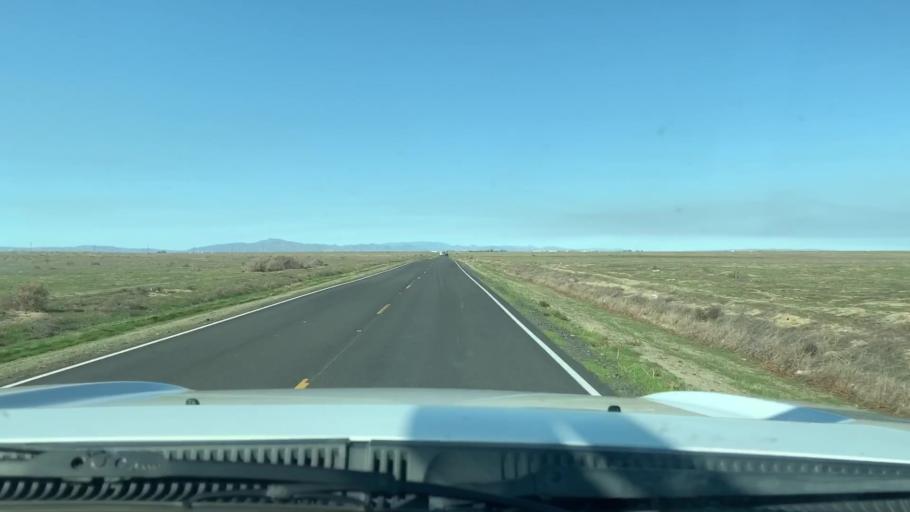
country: US
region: California
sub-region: Kern County
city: Lost Hills
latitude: 35.5742
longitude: -119.8176
